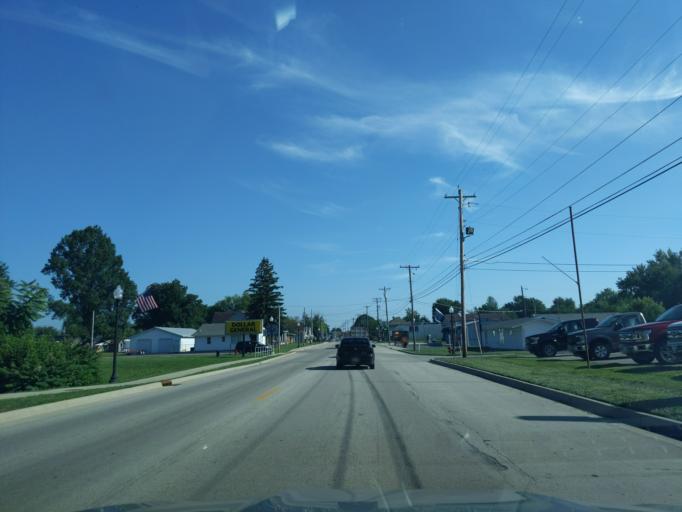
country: US
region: Indiana
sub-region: Ripley County
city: Osgood
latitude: 39.1364
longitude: -85.2937
